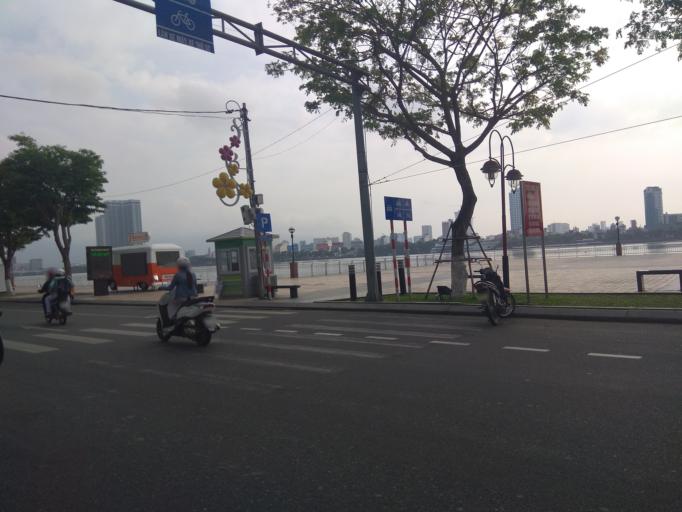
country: VN
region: Da Nang
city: Da Nang
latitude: 16.0616
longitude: 108.2241
